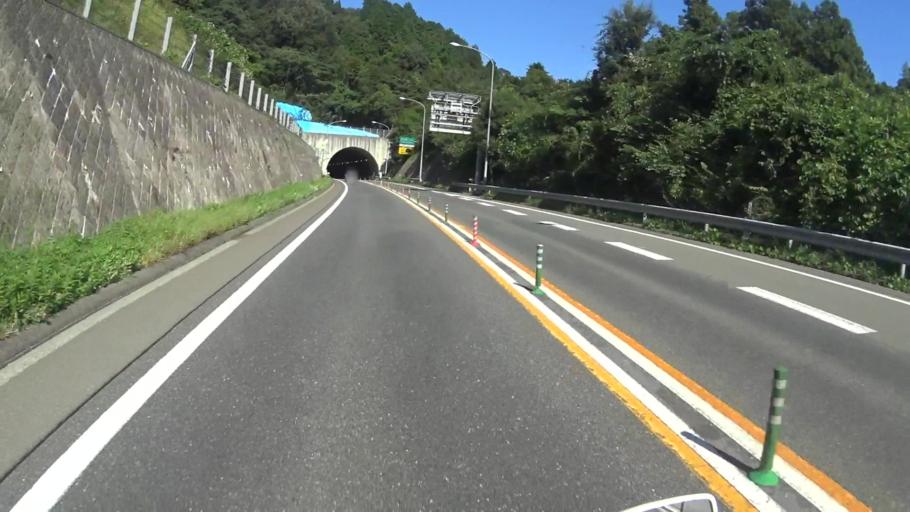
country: JP
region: Kyoto
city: Kameoka
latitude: 35.1241
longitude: 135.4787
